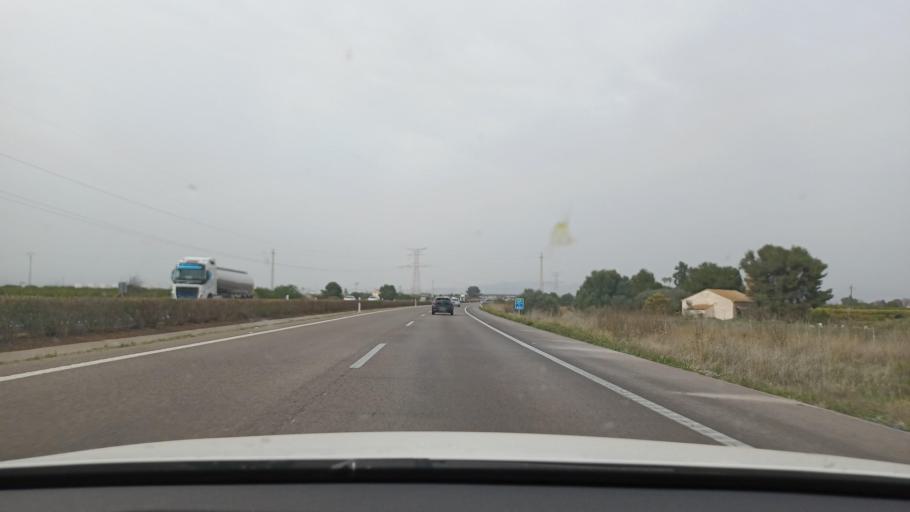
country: ES
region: Valencia
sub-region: Provincia de Castello
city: Alquerias del Nino Perdido
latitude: 39.9269
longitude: -0.1352
